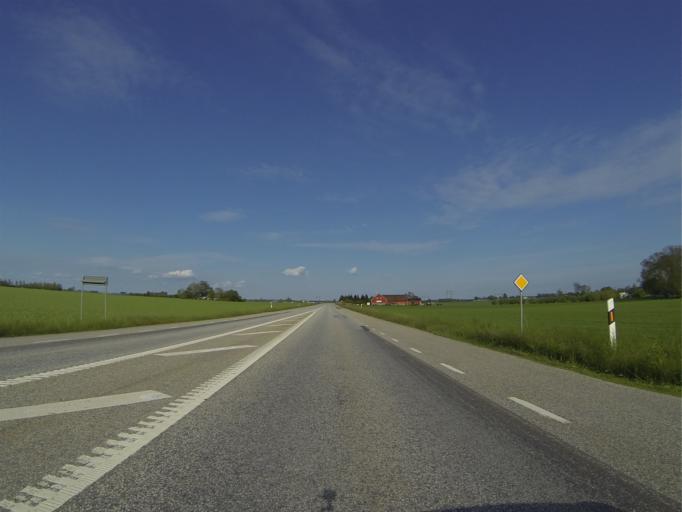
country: SE
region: Skane
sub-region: Staffanstorps Kommun
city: Hjaerup
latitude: 55.6419
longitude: 13.1496
